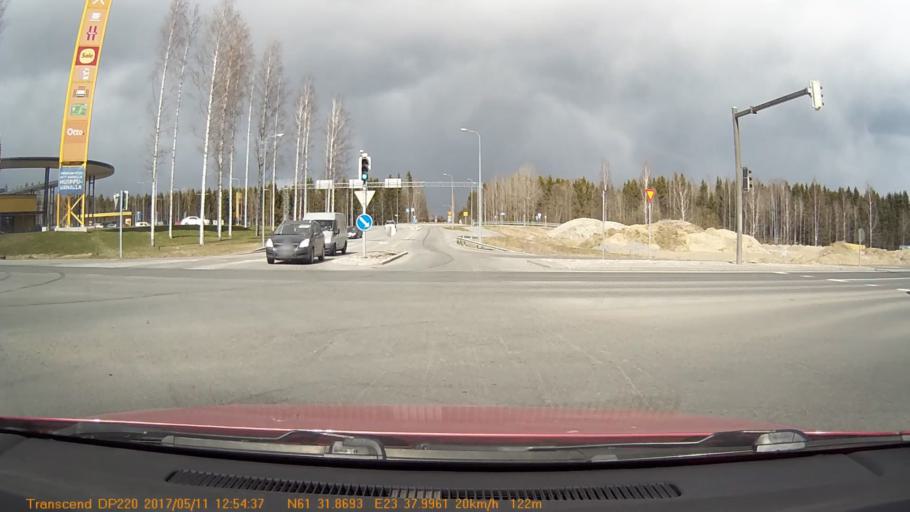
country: FI
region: Pirkanmaa
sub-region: Tampere
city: Yloejaervi
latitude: 61.5312
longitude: 23.6334
